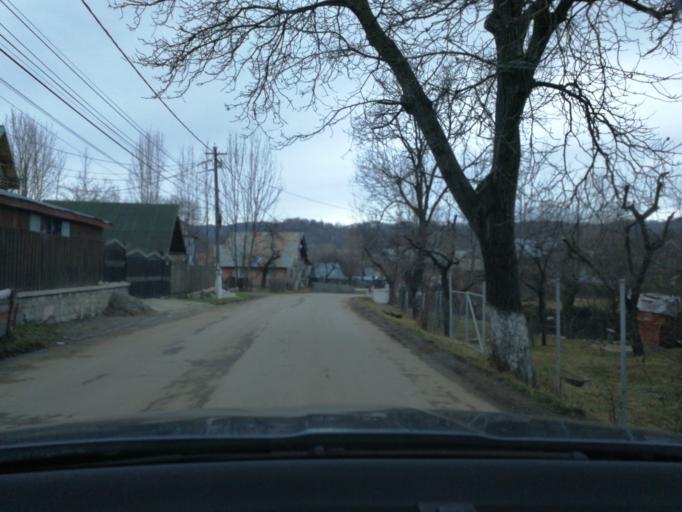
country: RO
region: Prahova
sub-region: Comuna Adunati
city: Ocina de Sus
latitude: 45.1841
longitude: 25.6075
